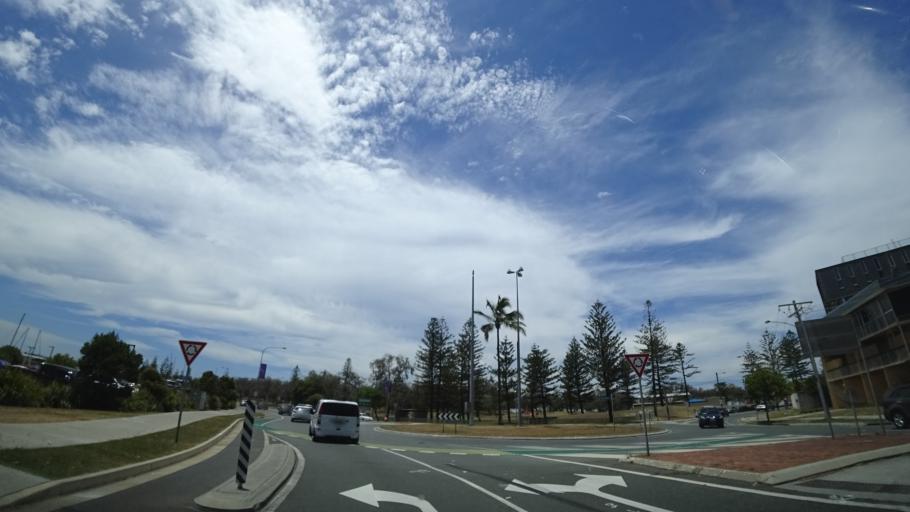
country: AU
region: Queensland
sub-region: Gold Coast
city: Main Beach
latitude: -27.9742
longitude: 153.4272
